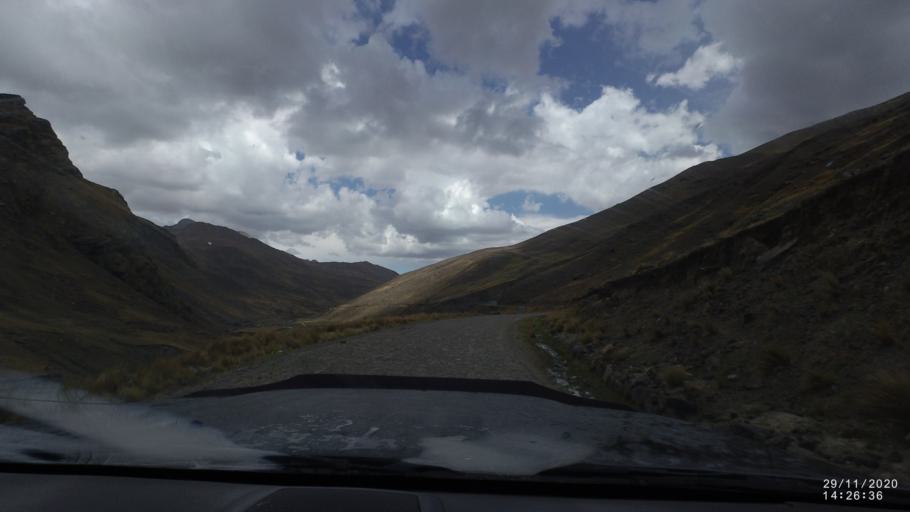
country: BO
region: Cochabamba
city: Sipe Sipe
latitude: -17.2579
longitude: -66.3697
